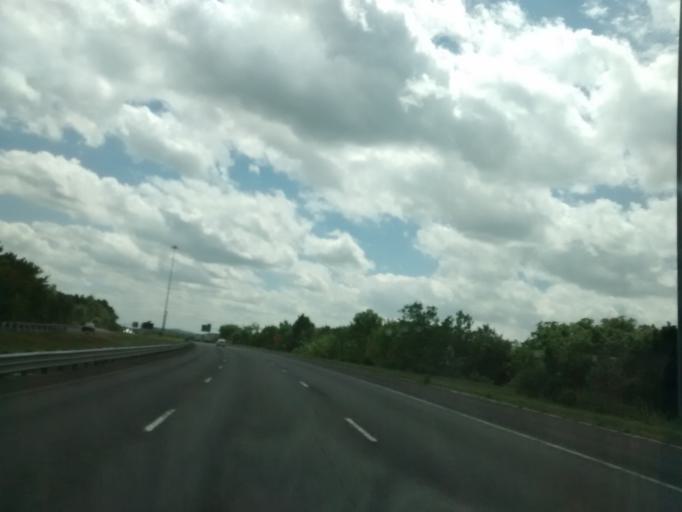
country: US
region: Massachusetts
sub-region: Worcester County
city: Sturbridge
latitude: 42.1119
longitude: -72.0817
